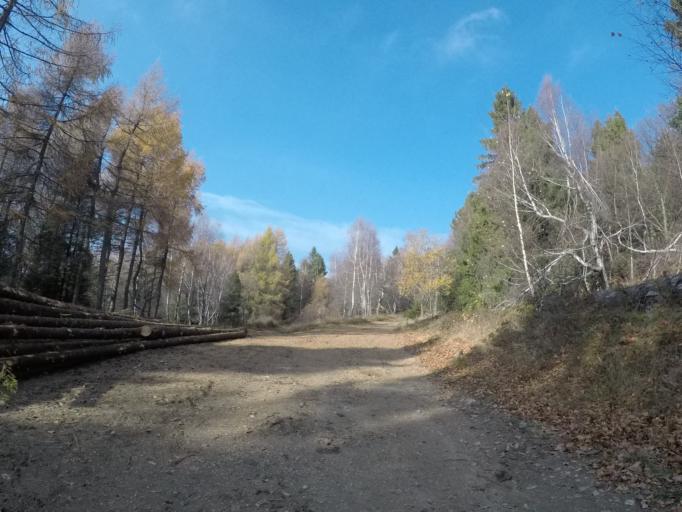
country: SK
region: Kosicky
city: Gelnica
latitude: 48.7621
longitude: 21.0332
